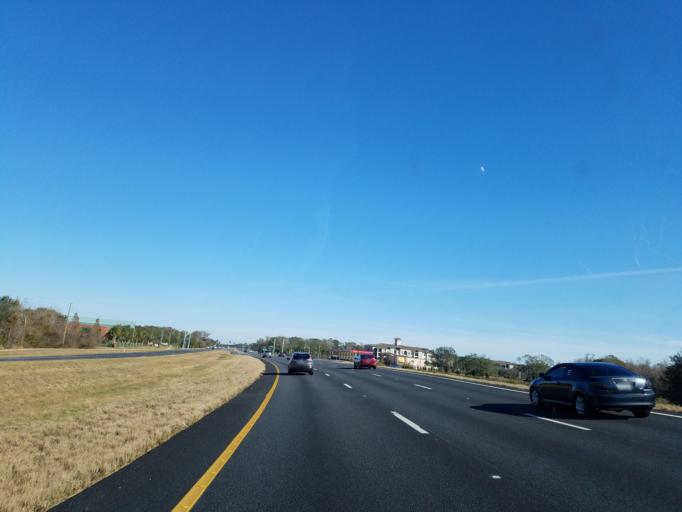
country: US
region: Florida
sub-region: Hillsborough County
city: Pebble Creek
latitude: 28.1852
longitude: -82.3697
